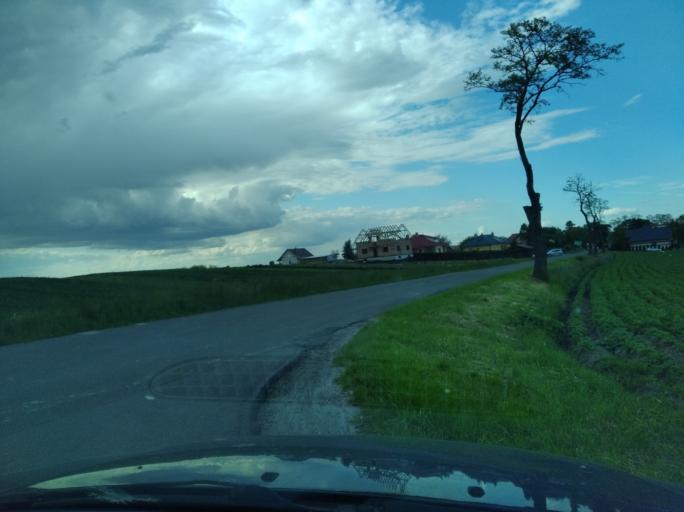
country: PL
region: Subcarpathian Voivodeship
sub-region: Powiat jaroslawski
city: Rokietnica
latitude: 49.9350
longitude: 22.6660
